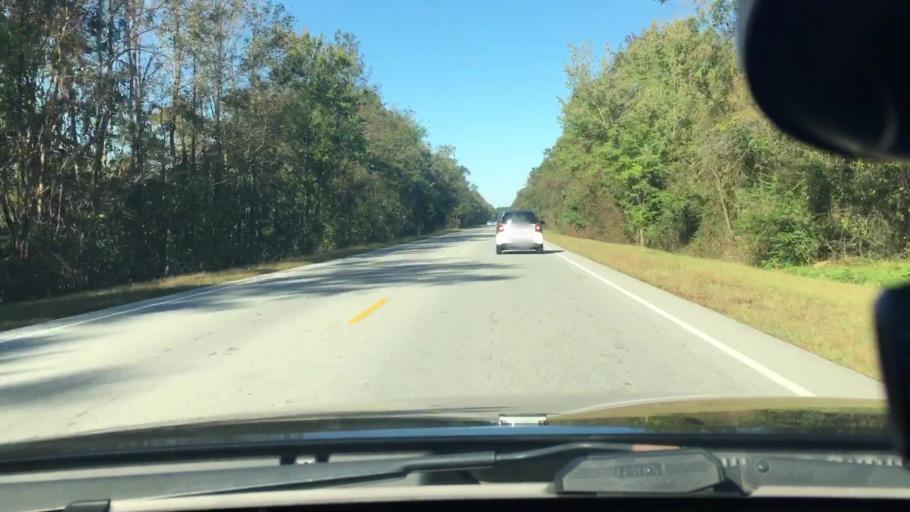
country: US
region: North Carolina
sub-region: Craven County
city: Vanceboro
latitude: 35.2009
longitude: -77.1295
